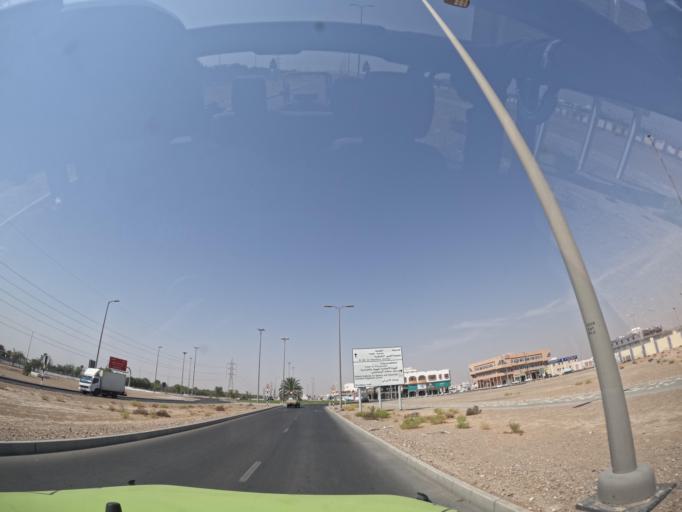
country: AE
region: Abu Dhabi
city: Al Ain
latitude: 24.2245
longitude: 55.5544
